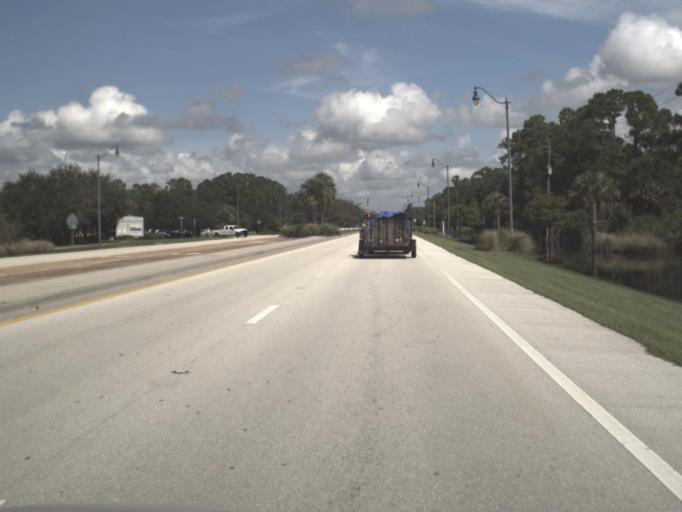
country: US
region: Florida
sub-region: Sarasota County
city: North Port
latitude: 27.0867
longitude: -82.1554
